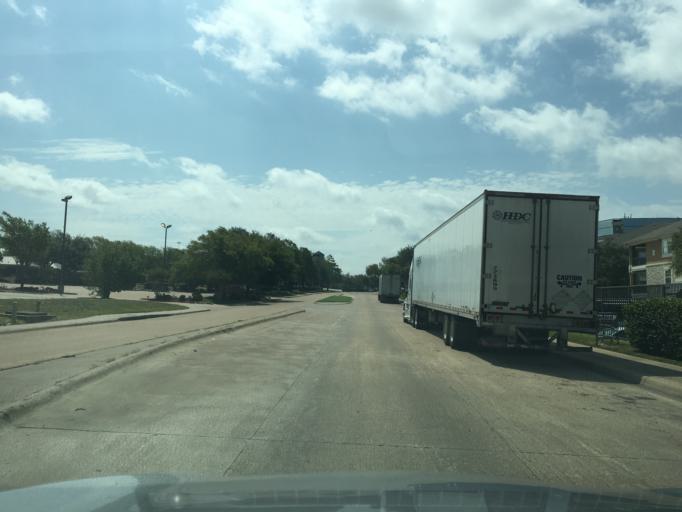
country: US
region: Texas
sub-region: Dallas County
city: Richardson
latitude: 32.9173
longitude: -96.7477
